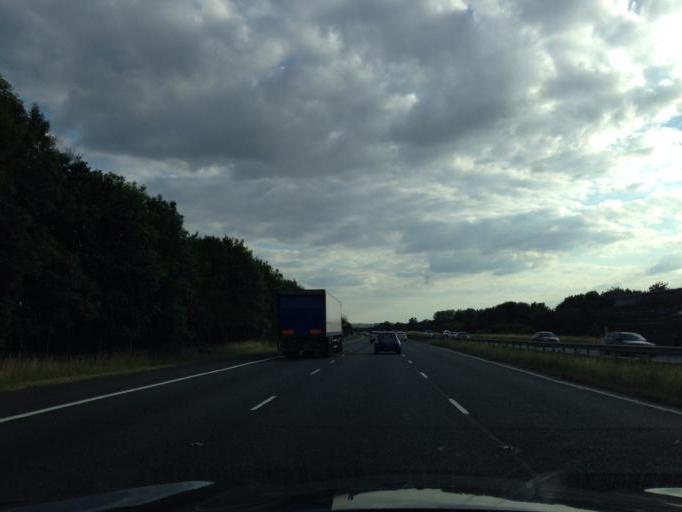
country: GB
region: England
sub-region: Oxfordshire
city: Wheatley
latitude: 51.7873
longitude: -1.0878
